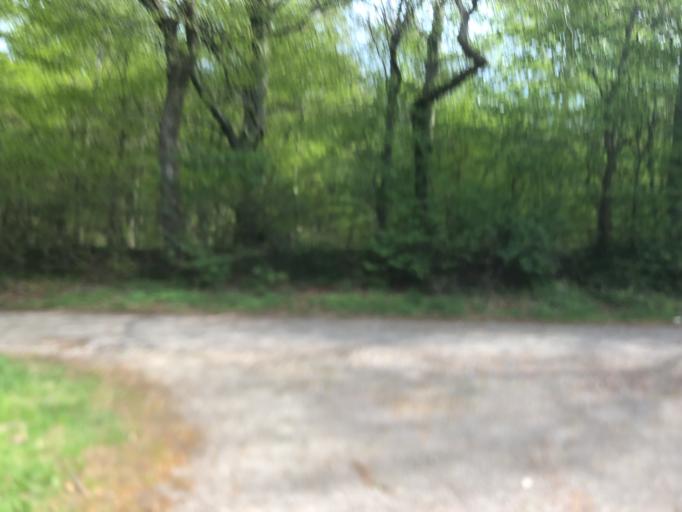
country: DK
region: Zealand
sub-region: Ringsted Kommune
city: Ringsted
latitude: 55.4499
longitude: 11.8286
